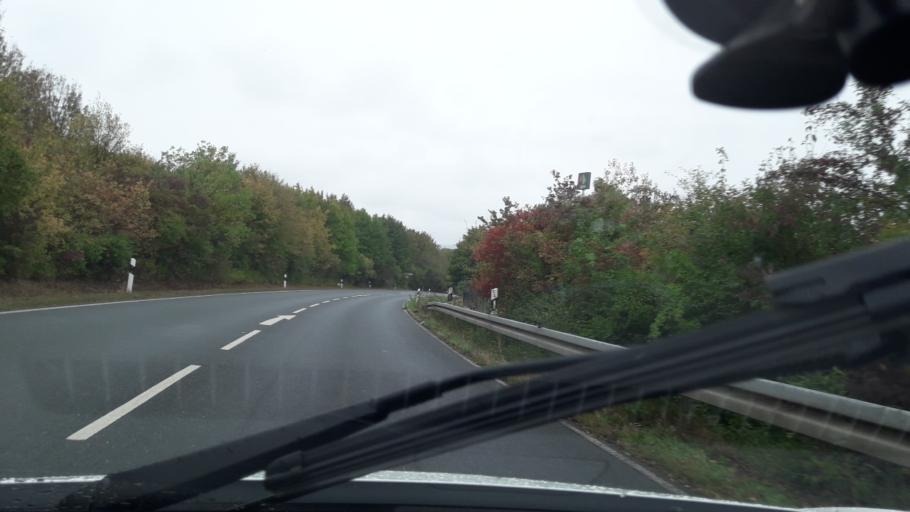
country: DE
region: Lower Saxony
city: Schladen
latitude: 52.0304
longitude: 10.5378
